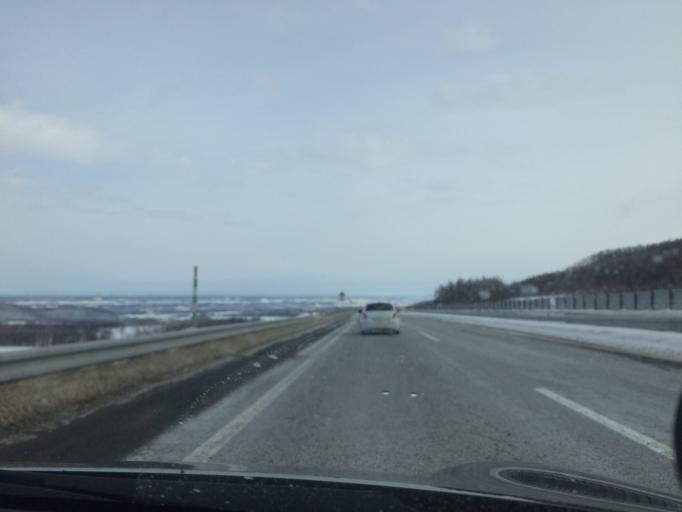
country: JP
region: Hokkaido
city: Otofuke
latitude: 43.0208
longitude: 142.8175
